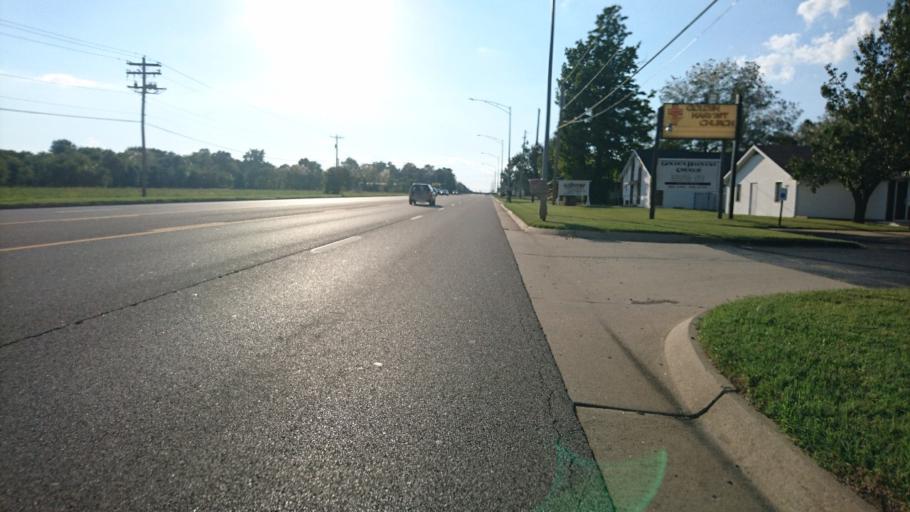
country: US
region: Missouri
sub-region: Greene County
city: Springfield
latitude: 37.2124
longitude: -93.3681
